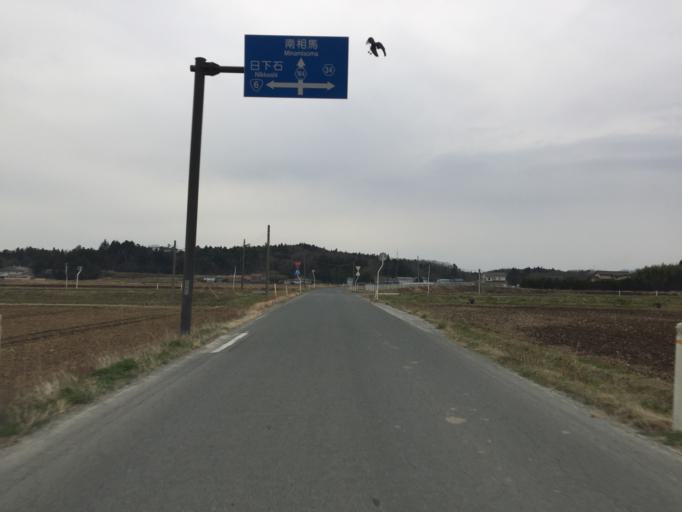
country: JP
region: Miyagi
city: Marumori
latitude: 37.7610
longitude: 140.9390
